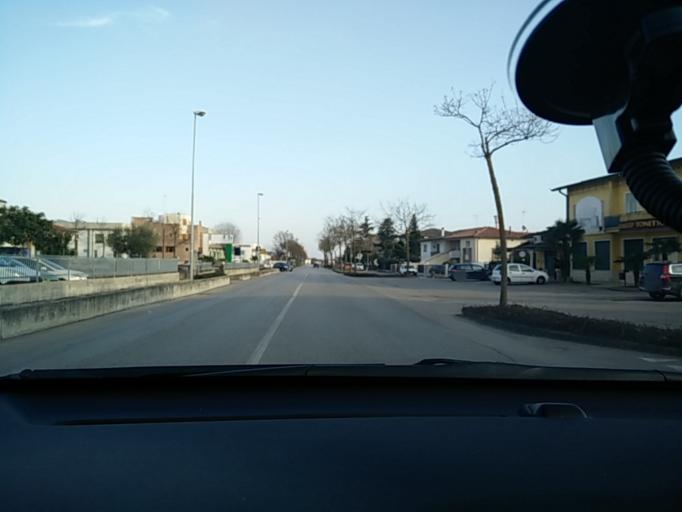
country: IT
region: Veneto
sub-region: Provincia di Venezia
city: San Dona di Piave
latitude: 45.6232
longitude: 12.5868
